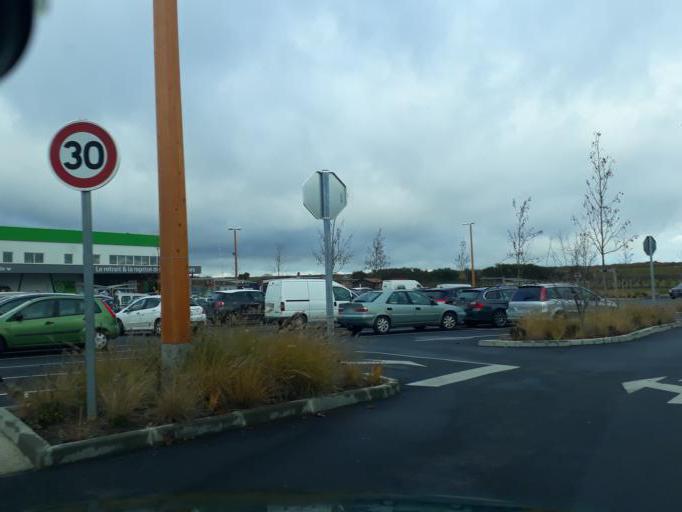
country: FR
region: Centre
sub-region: Departement du Loir-et-Cher
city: Villebarou
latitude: 47.6153
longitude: 1.3224
